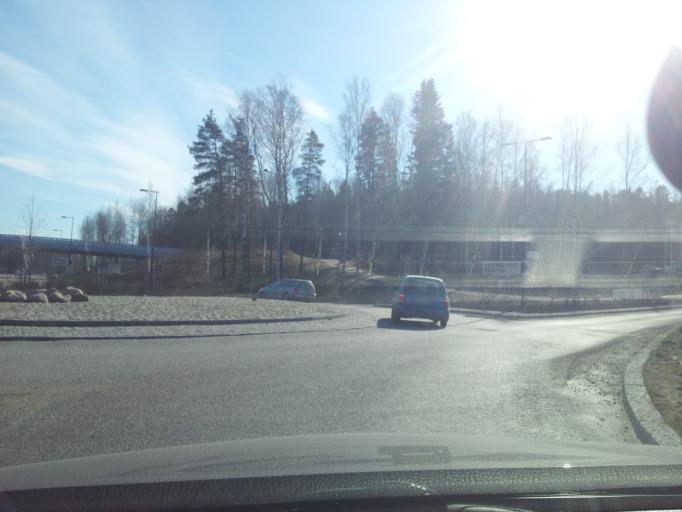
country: FI
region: Uusimaa
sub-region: Helsinki
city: Espoo
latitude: 60.1691
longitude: 24.6203
